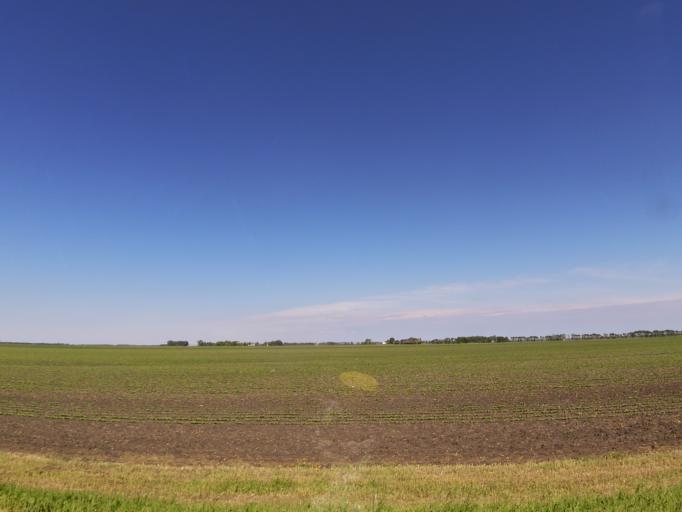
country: US
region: North Dakota
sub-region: Walsh County
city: Grafton
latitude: 48.3471
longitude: -97.2558
